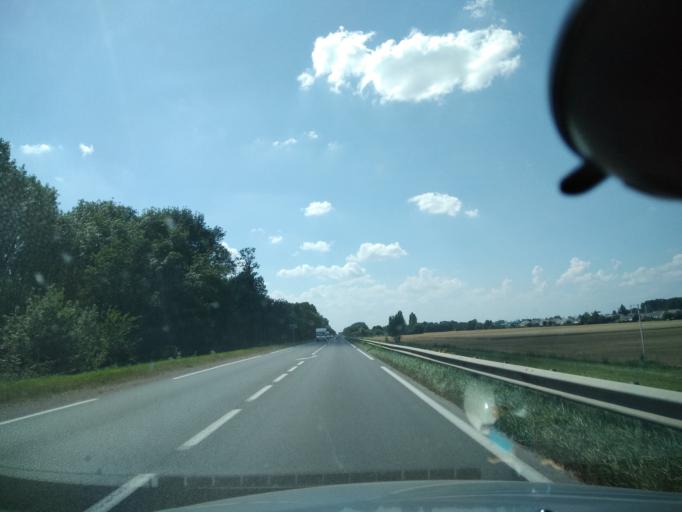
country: FR
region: Centre
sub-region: Departement d'Indre-et-Loire
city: Larcay
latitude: 47.3812
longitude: 0.7800
